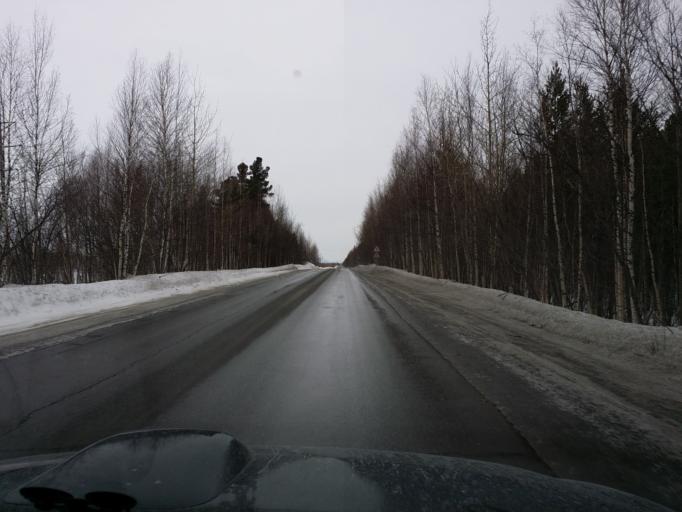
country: RU
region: Tomsk
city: Strezhevoy
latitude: 60.8001
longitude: 77.2973
